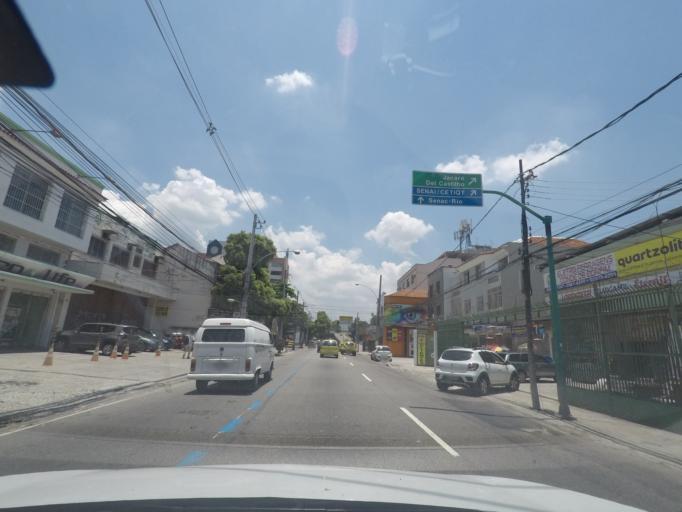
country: BR
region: Rio de Janeiro
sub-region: Rio De Janeiro
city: Rio de Janeiro
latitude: -22.9023
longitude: -43.2573
